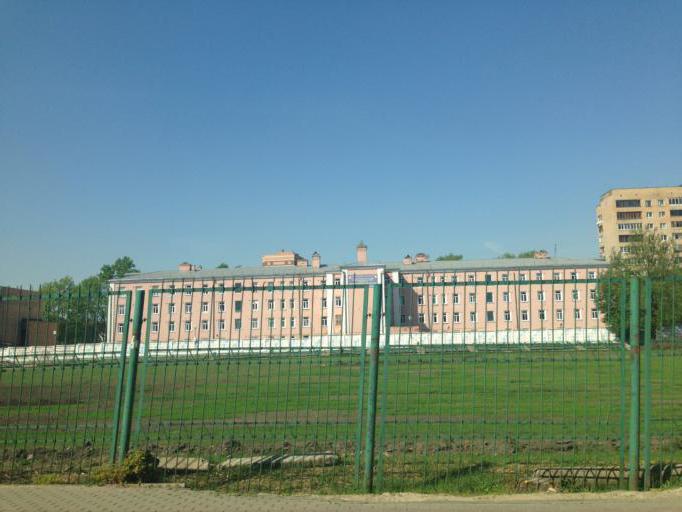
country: RU
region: Moskovskaya
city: Balashikha
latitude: 55.8155
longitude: 37.9668
